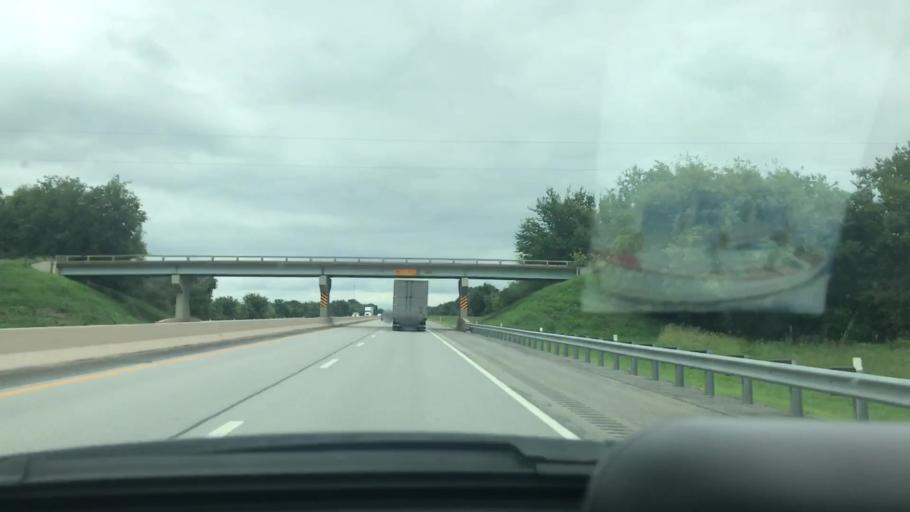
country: US
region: Oklahoma
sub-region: Ottawa County
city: Commerce
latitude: 36.9025
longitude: -94.8066
